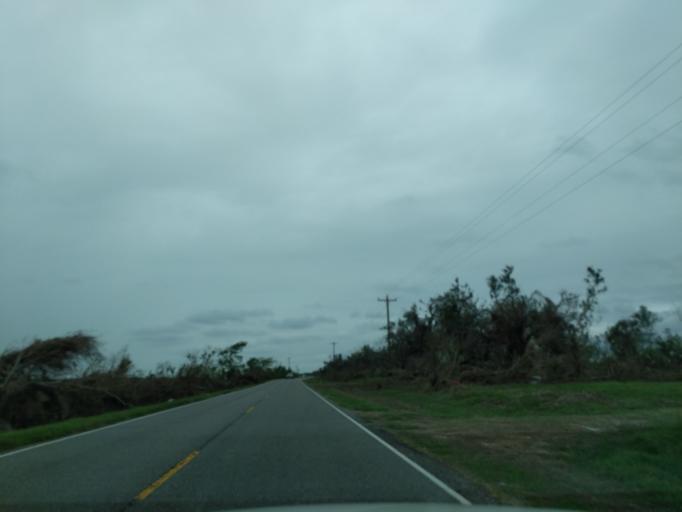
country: US
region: Louisiana
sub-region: Cameron Parish
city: Cameron
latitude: 29.7868
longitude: -93.1406
